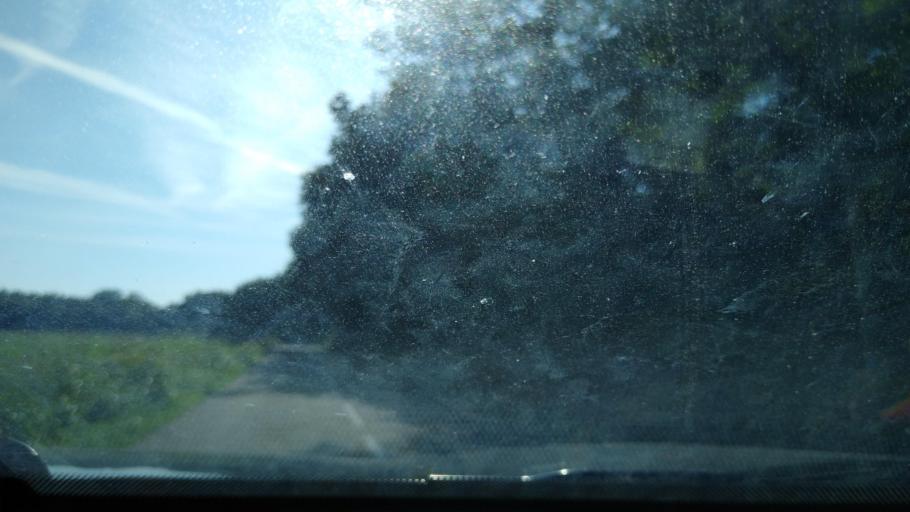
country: FR
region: Midi-Pyrenees
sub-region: Departement de la Haute-Garonne
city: Montaigut-sur-Save
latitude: 43.7331
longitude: 1.2400
